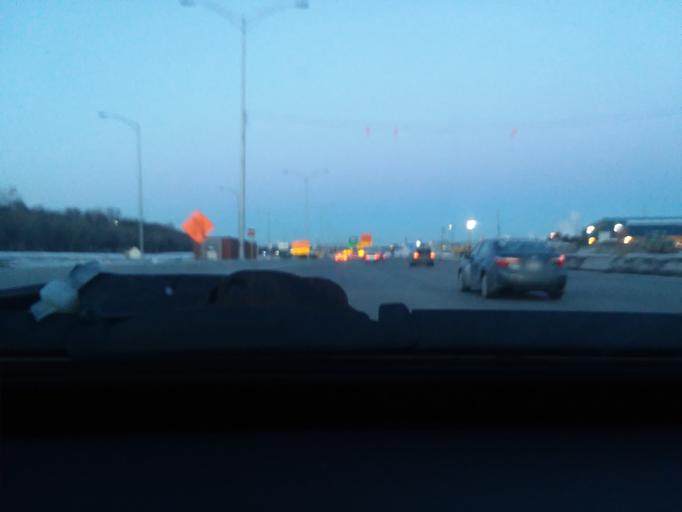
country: CA
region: Quebec
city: Saint-Raymond
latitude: 45.4609
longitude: -73.6163
